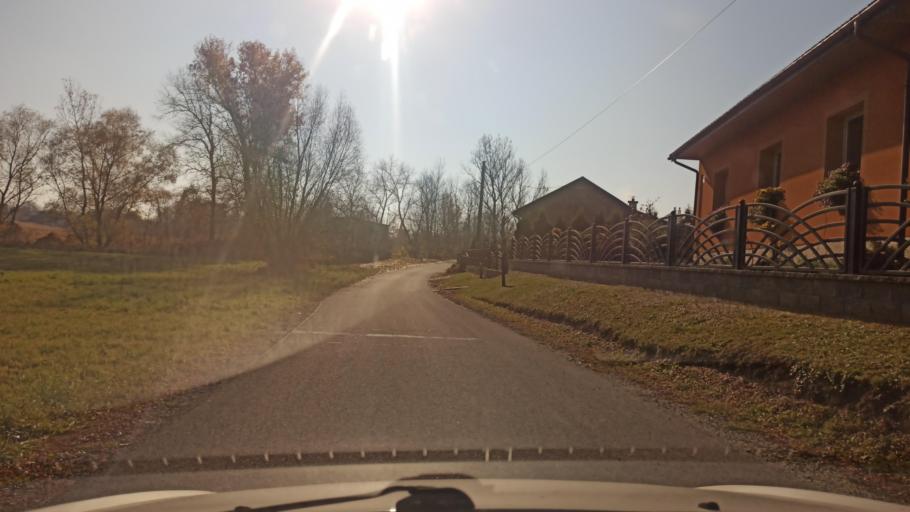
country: PL
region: Subcarpathian Voivodeship
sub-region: Powiat jaroslawski
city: Radymno
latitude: 49.9360
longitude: 22.8121
